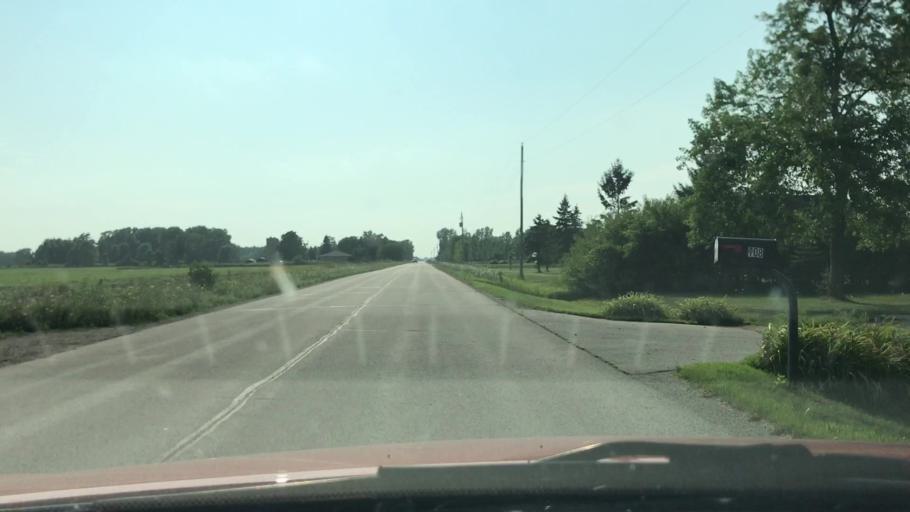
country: US
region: Wisconsin
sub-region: Brown County
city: Oneida
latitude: 44.4298
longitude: -88.1600
